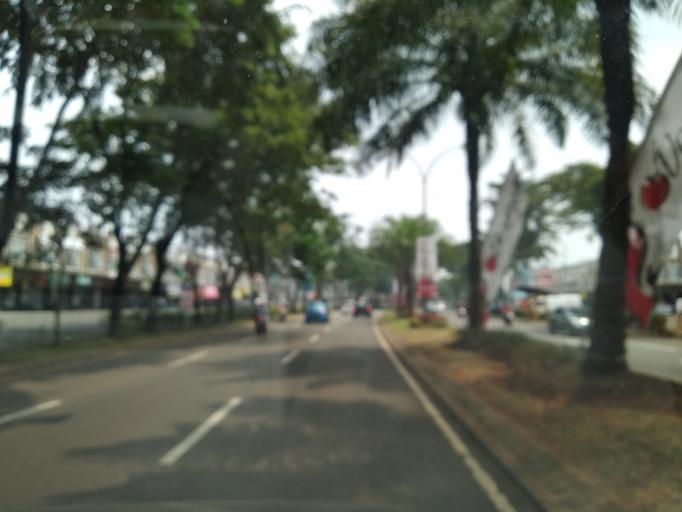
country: ID
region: West Java
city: Bekasi
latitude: -6.2881
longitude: 107.0432
